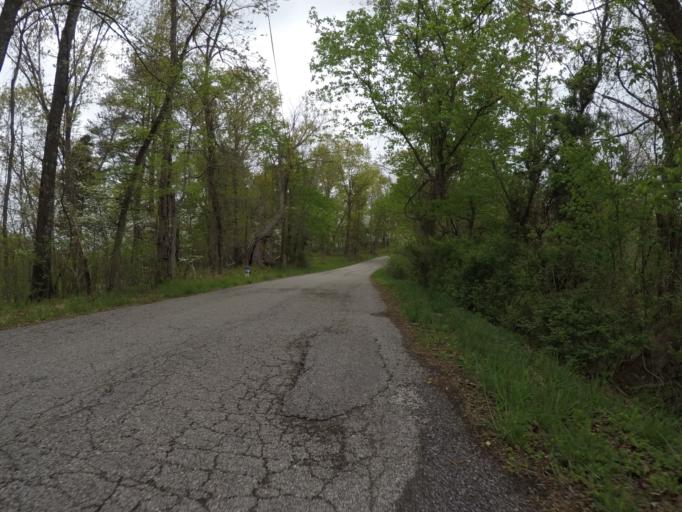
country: US
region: West Virginia
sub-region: Cabell County
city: Barboursville
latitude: 38.3968
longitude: -82.2542
